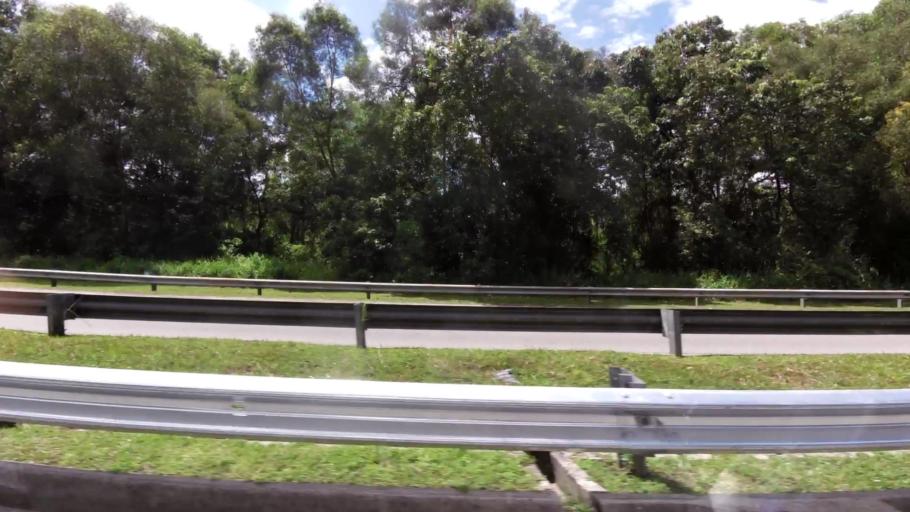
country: BN
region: Brunei and Muara
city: Bandar Seri Begawan
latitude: 4.9482
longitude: 114.9170
